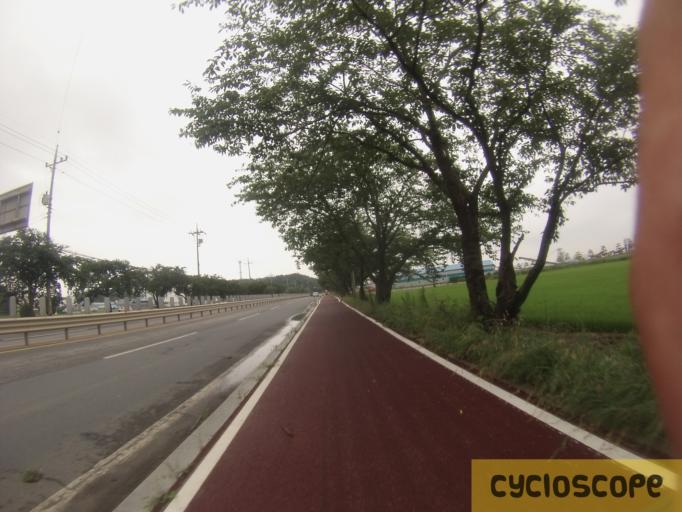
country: KR
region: Chungcheongnam-do
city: Taisen-ri
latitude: 36.1625
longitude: 126.5258
